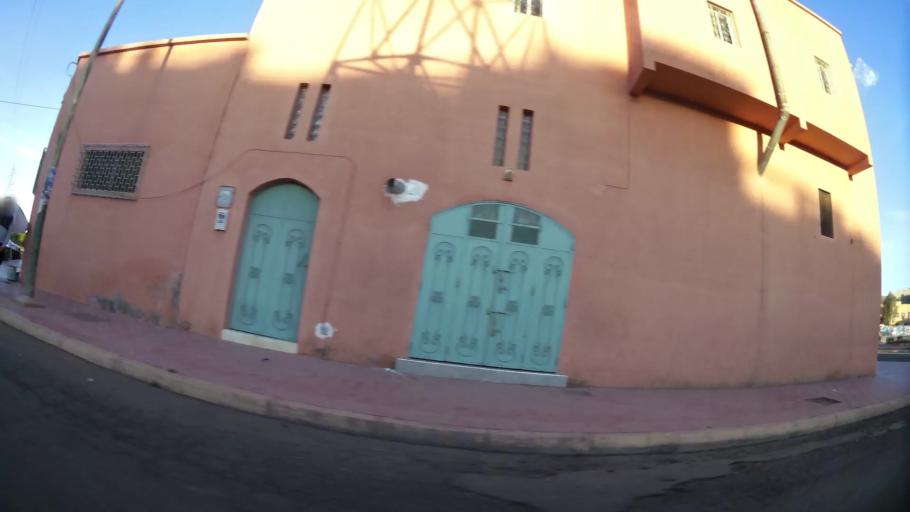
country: MA
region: Marrakech-Tensift-Al Haouz
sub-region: Marrakech
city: Marrakesh
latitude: 31.6536
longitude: -8.0320
